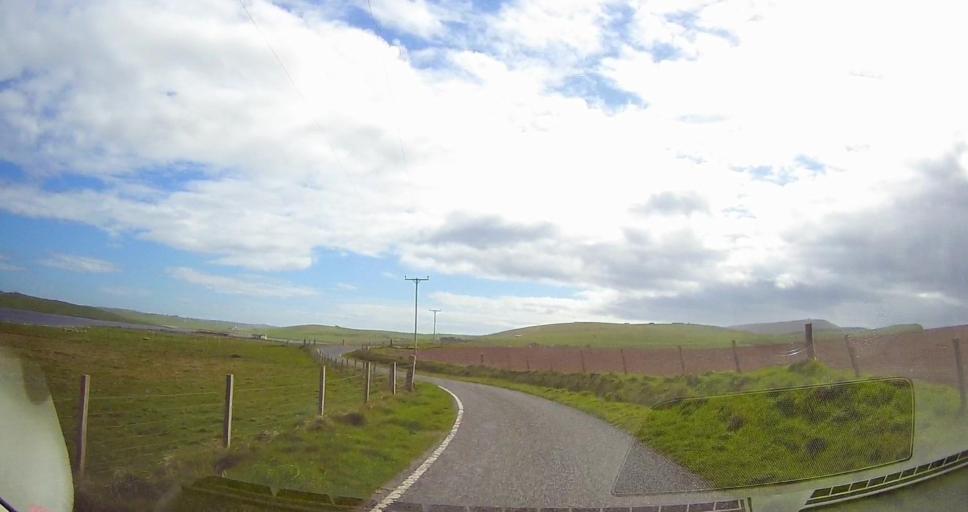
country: GB
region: Scotland
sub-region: Shetland Islands
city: Sandwick
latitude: 59.9404
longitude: -1.3463
